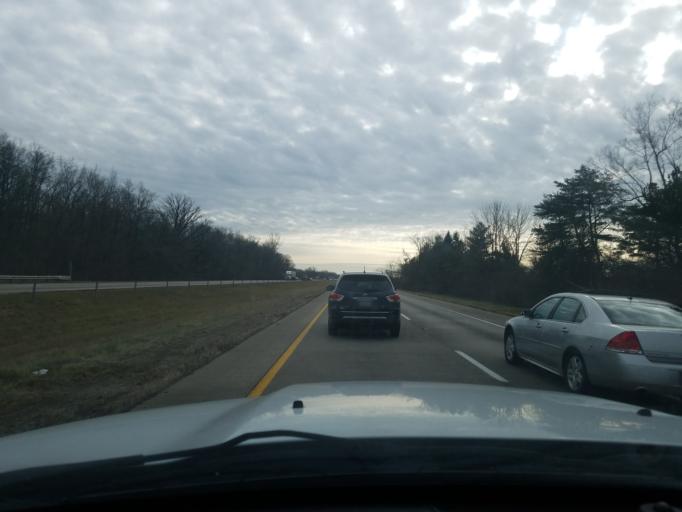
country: US
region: Indiana
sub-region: Delaware County
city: Yorktown
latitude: 40.2577
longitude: -85.5577
